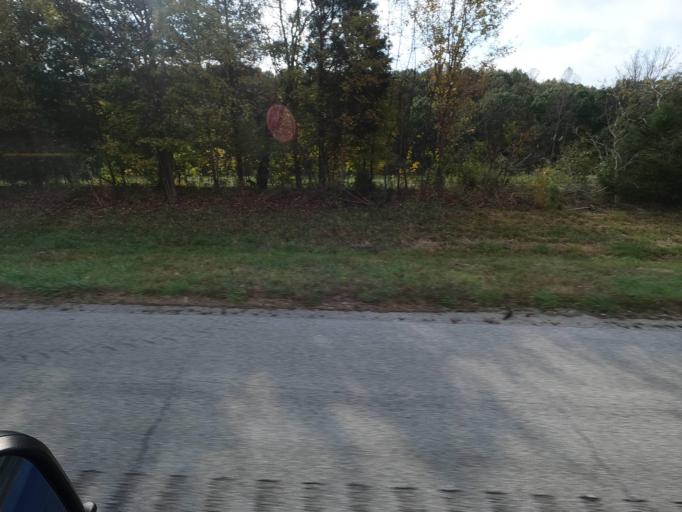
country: US
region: Tennessee
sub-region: Dickson County
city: Burns
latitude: 36.0173
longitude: -87.2463
